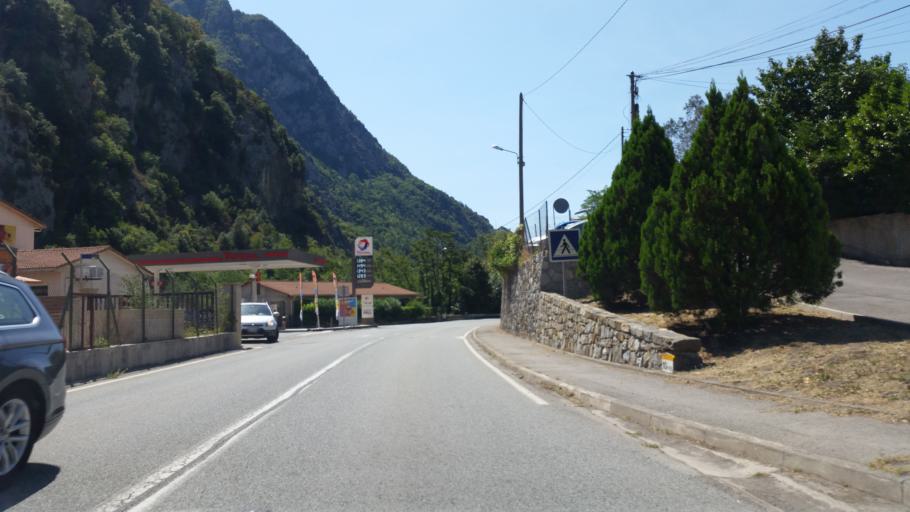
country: FR
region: Provence-Alpes-Cote d'Azur
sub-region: Departement des Alpes-Maritimes
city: Breil-sur-Roya
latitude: 43.9560
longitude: 7.5209
